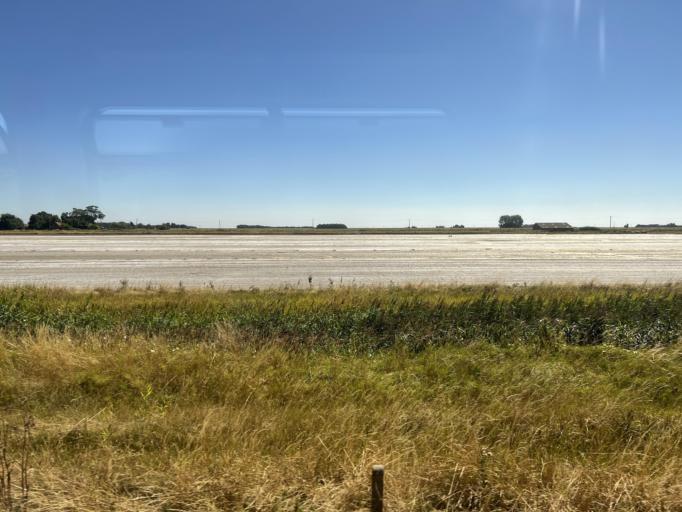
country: GB
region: England
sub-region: Lincolnshire
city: Wainfleet All Saints
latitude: 53.1098
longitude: 0.2582
